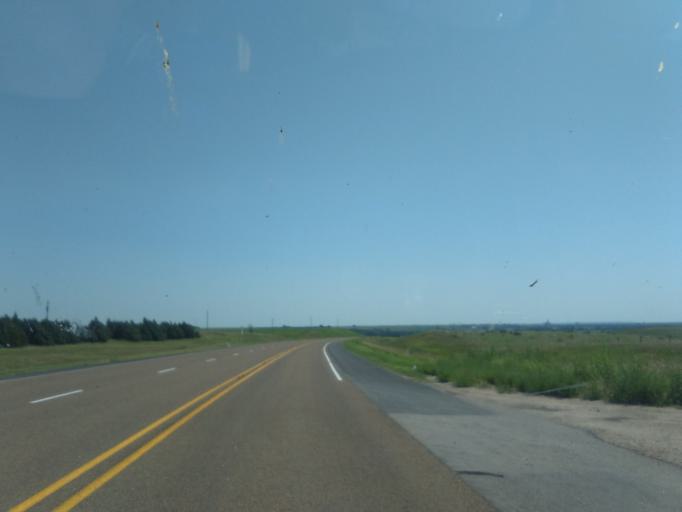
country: US
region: Nebraska
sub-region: Hitchcock County
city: Trenton
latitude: 40.2336
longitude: -100.9097
